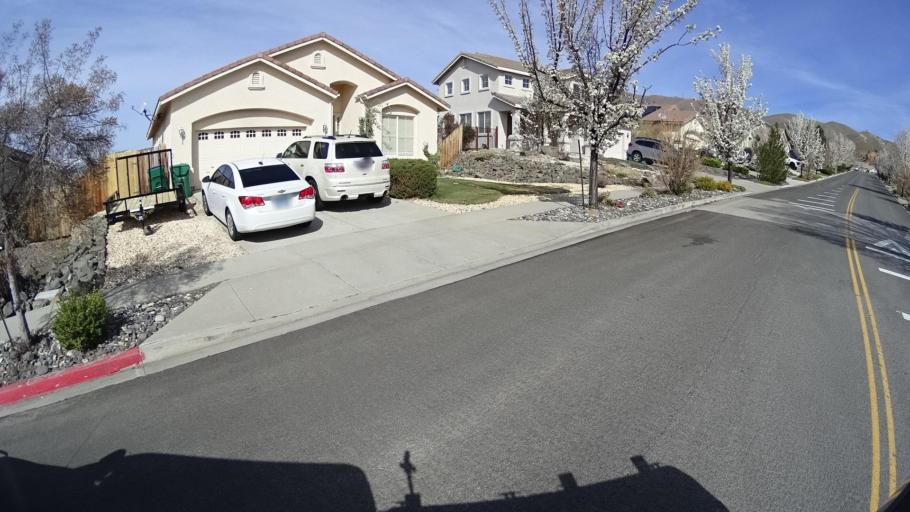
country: US
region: Nevada
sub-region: Washoe County
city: Mogul
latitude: 39.5416
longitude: -119.9102
